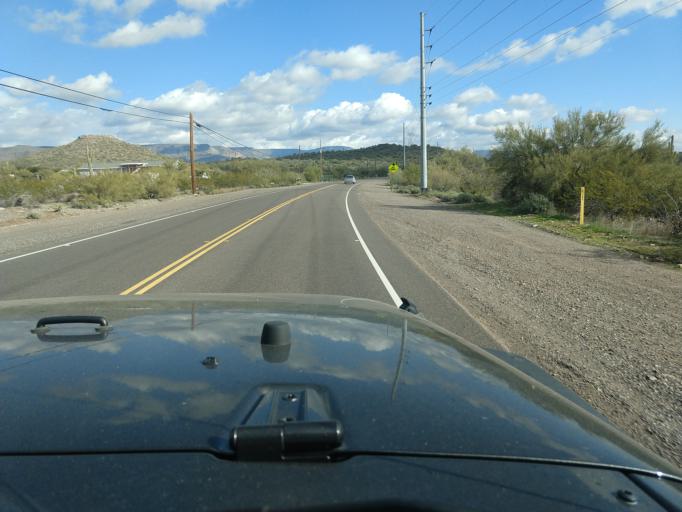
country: US
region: Arizona
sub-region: Maricopa County
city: New River
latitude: 33.9227
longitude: -112.1119
